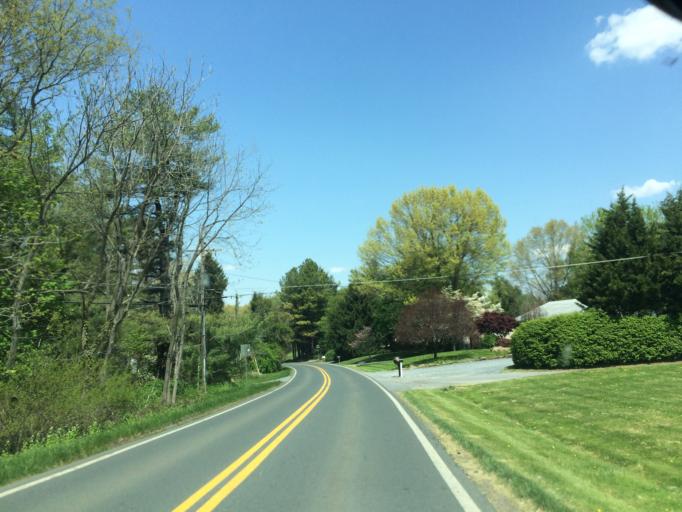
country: US
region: Maryland
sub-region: Carroll County
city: Eldersburg
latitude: 39.4346
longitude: -76.9919
